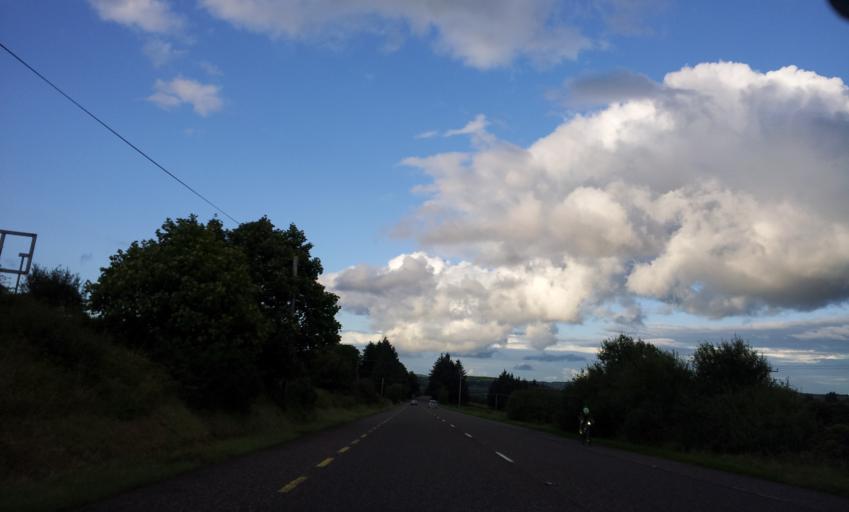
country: IE
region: Munster
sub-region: Ciarrai
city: Castleisland
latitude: 52.2902
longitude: -9.4001
